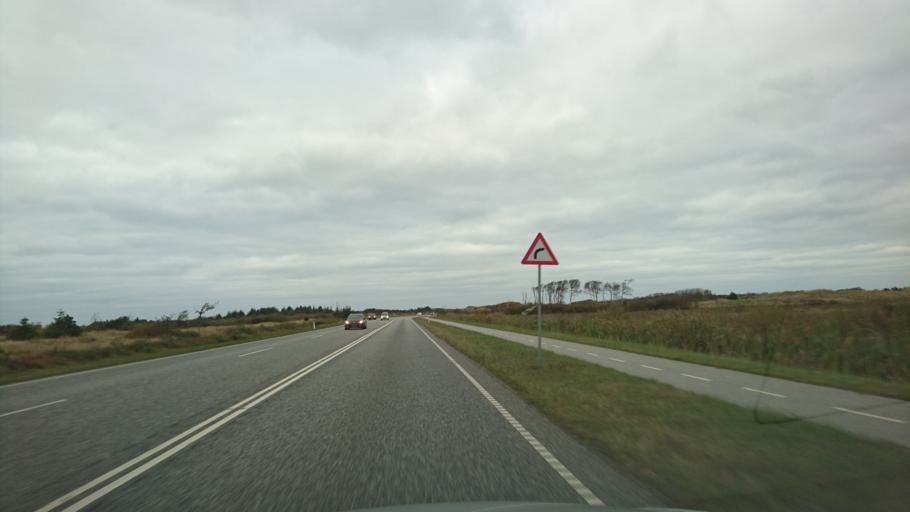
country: DK
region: North Denmark
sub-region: Frederikshavn Kommune
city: Skagen
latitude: 57.6684
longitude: 10.4545
